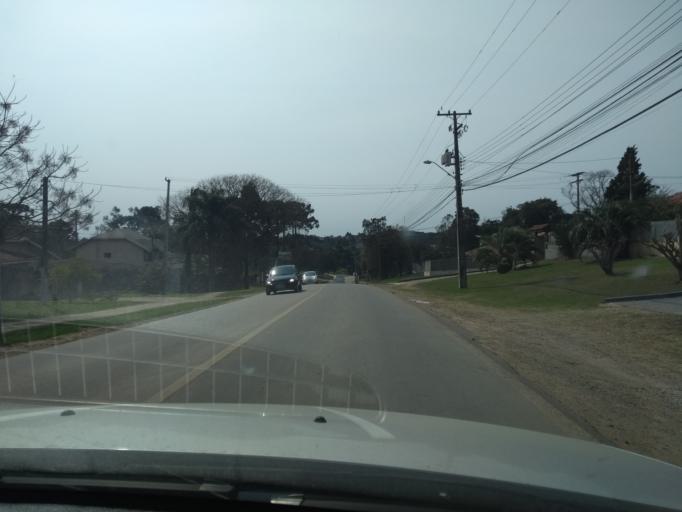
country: BR
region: Parana
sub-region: Araucaria
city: Araucaria
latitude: -25.6147
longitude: -49.3426
